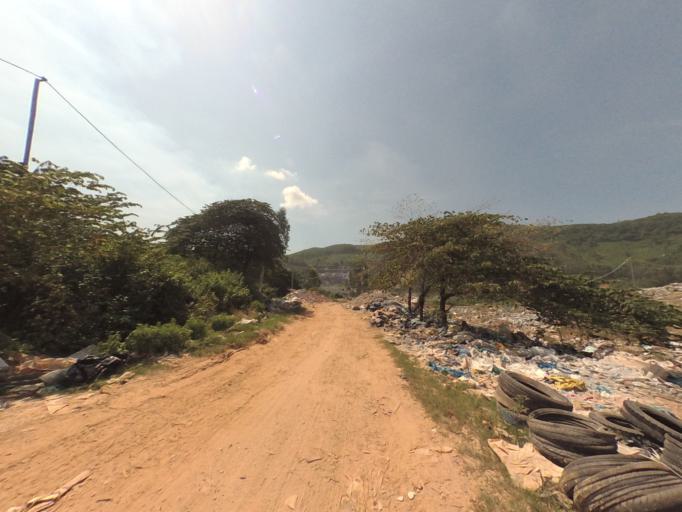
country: VN
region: Da Nang
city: Lien Chieu
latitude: 16.0420
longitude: 108.1433
